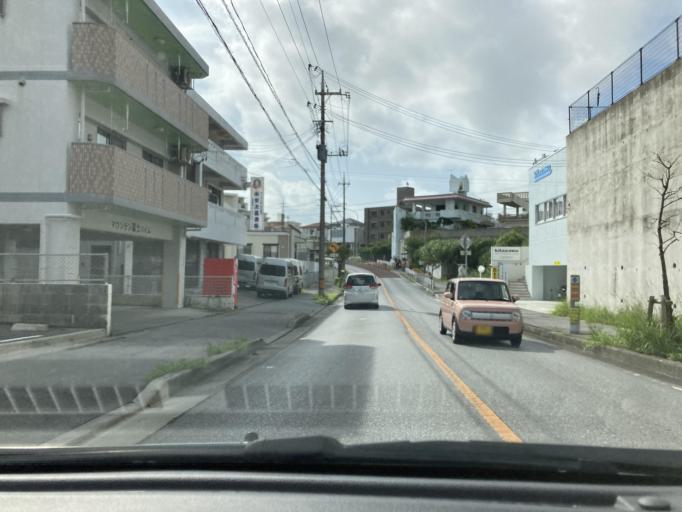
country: JP
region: Okinawa
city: Ginowan
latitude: 26.2573
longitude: 127.7689
